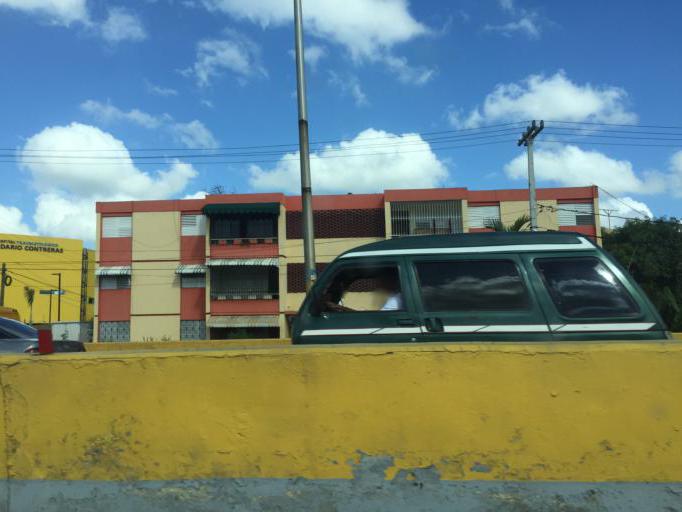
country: DO
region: Santo Domingo
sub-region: Santo Domingo
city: Santo Domingo Este
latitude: 18.4847
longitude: -69.8623
